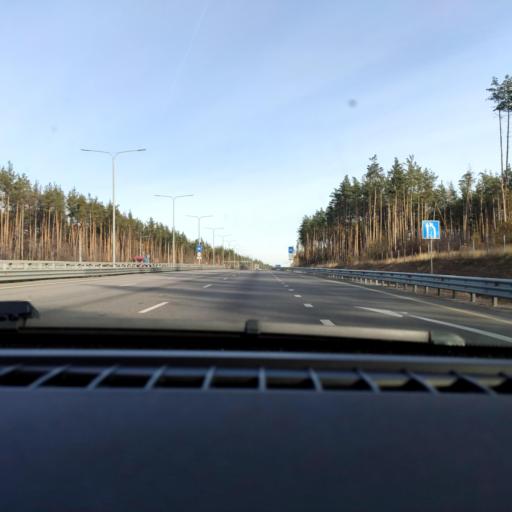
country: RU
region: Voronezj
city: Somovo
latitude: 51.6932
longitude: 39.3035
